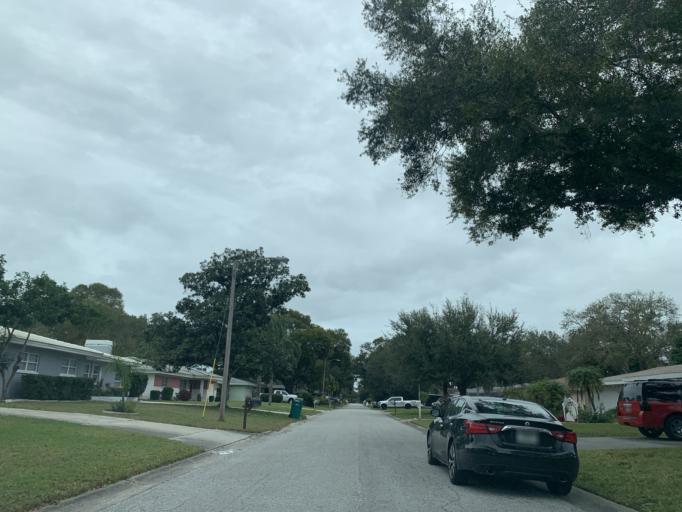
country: US
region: Florida
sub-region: Pinellas County
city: Belleair
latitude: 27.9355
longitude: -82.7803
